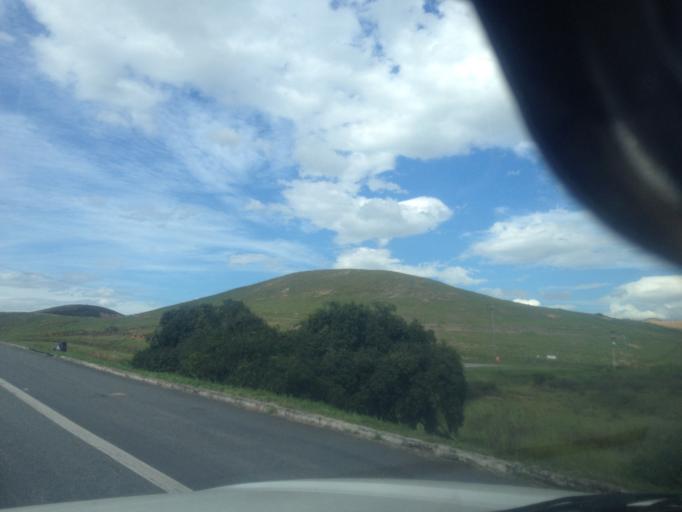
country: BR
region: Rio de Janeiro
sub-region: Porto Real
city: Porto Real
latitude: -22.4501
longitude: -44.3295
